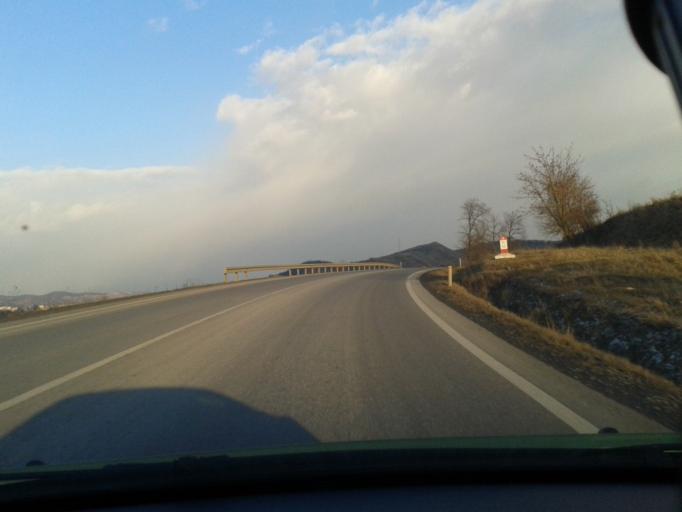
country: RO
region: Sibiu
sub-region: Comuna Tarnava
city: Tarnava
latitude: 46.1266
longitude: 24.2891
